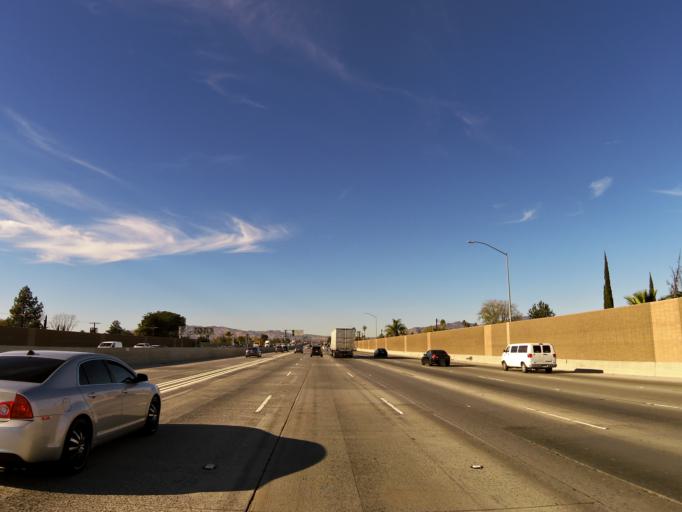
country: US
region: California
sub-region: Los Angeles County
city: San Fernando
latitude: 34.2402
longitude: -118.4174
